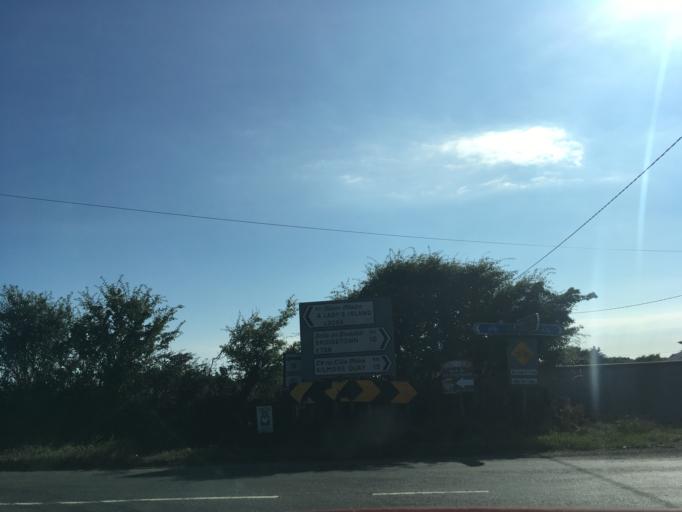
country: IE
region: Leinster
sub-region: Loch Garman
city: Rosslare
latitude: 52.2355
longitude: -6.4122
